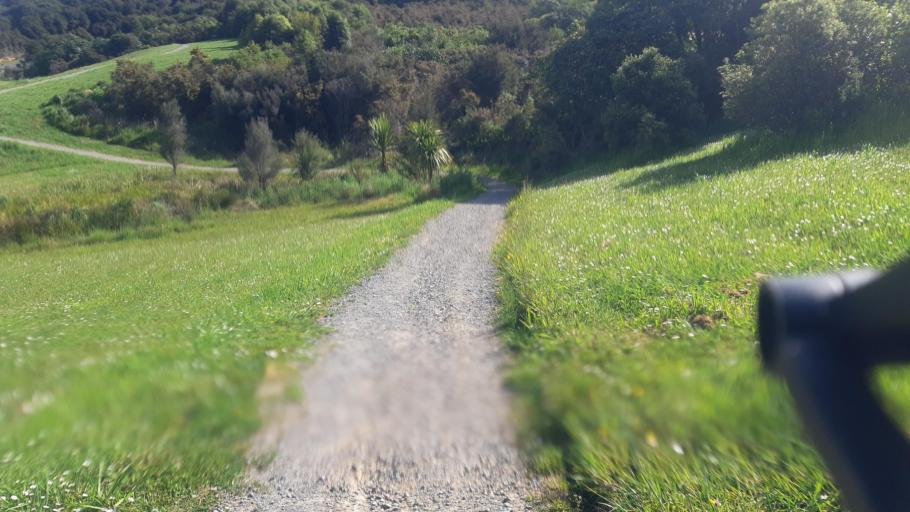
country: NZ
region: Marlborough
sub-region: Marlborough District
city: Picton
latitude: -41.2751
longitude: 174.0220
